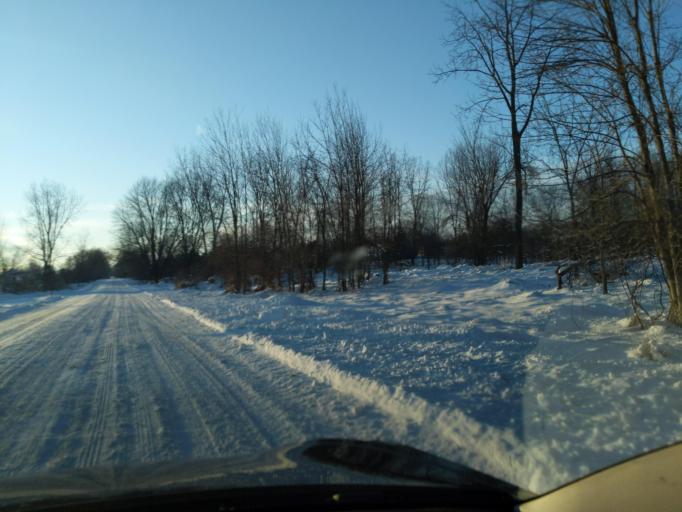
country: US
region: Michigan
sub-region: Livingston County
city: Fowlerville
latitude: 42.5680
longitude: -84.1267
